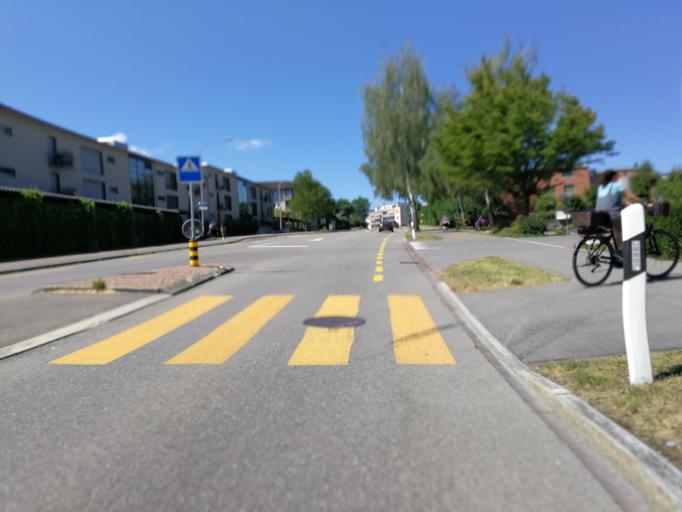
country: CH
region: Zurich
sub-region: Bezirk Uster
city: Uster / Nieder-Uster
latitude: 47.3507
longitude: 8.7035
